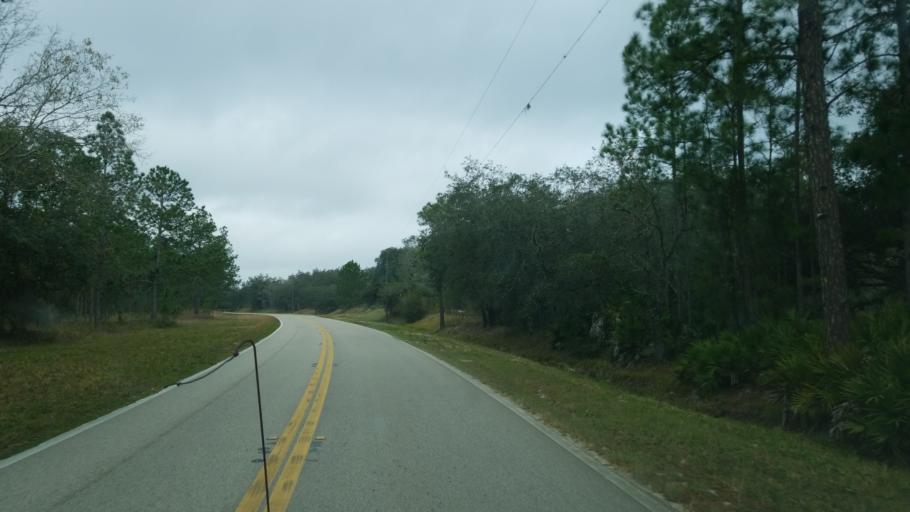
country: US
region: Florida
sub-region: Lake County
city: Four Corners
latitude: 28.2610
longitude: -81.7196
